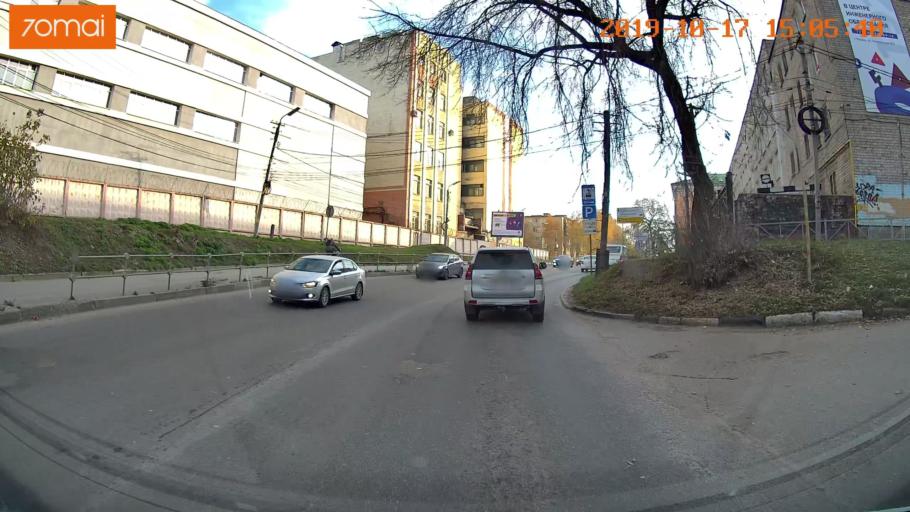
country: RU
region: Rjazan
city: Ryazan'
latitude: 54.6339
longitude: 39.7243
